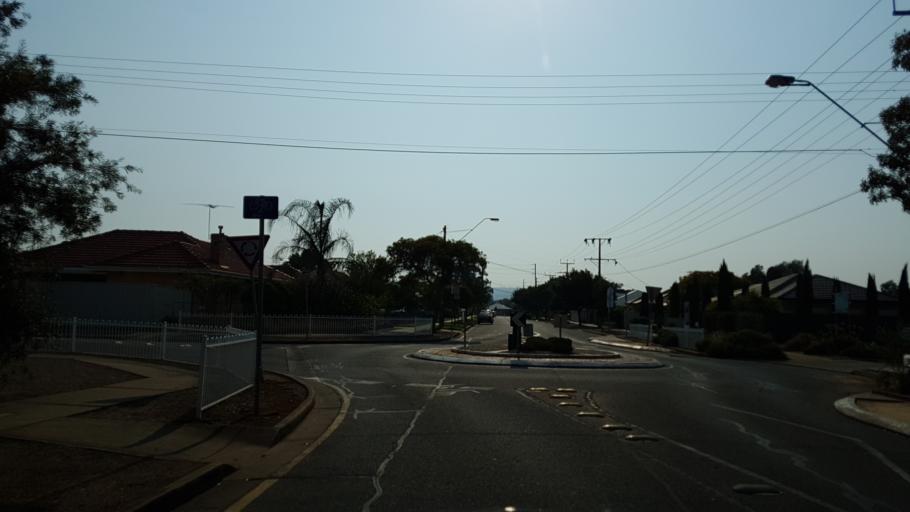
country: AU
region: South Australia
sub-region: Holdfast Bay
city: North Brighton
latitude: -35.0032
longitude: 138.5371
